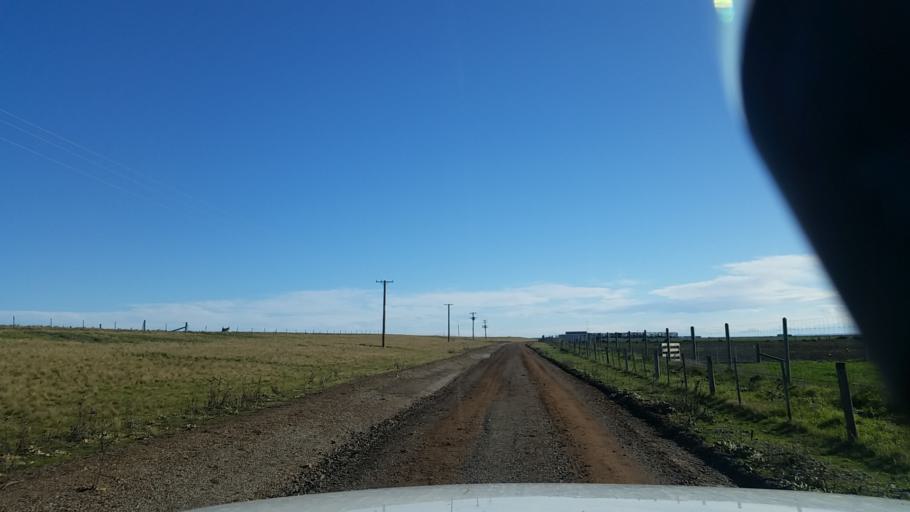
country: NZ
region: Canterbury
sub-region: Selwyn District
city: Lincoln
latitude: -43.8122
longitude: 172.6560
